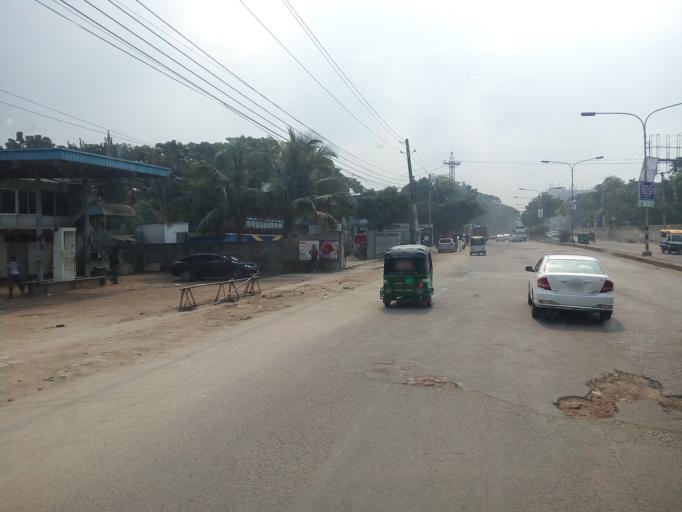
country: BD
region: Dhaka
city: Azimpur
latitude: 23.7823
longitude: 90.3505
